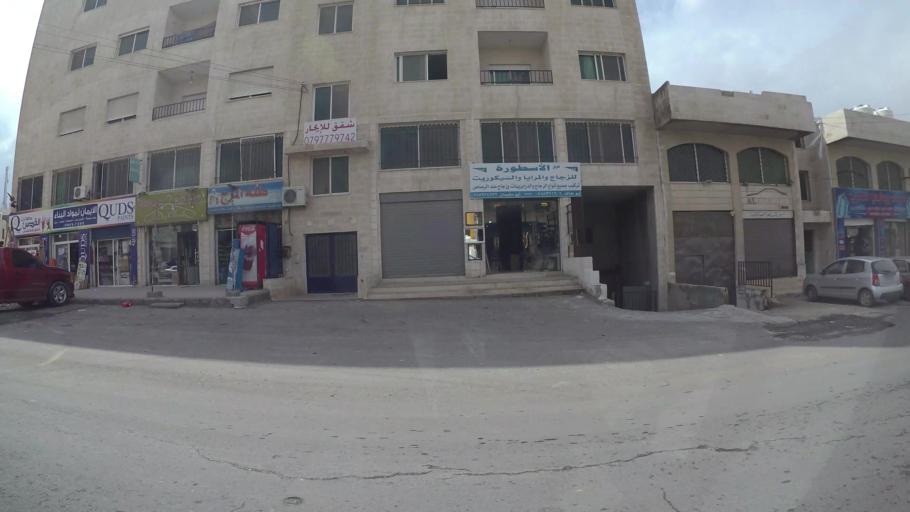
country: JO
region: Amman
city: Umm as Summaq
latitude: 31.8996
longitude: 35.8379
